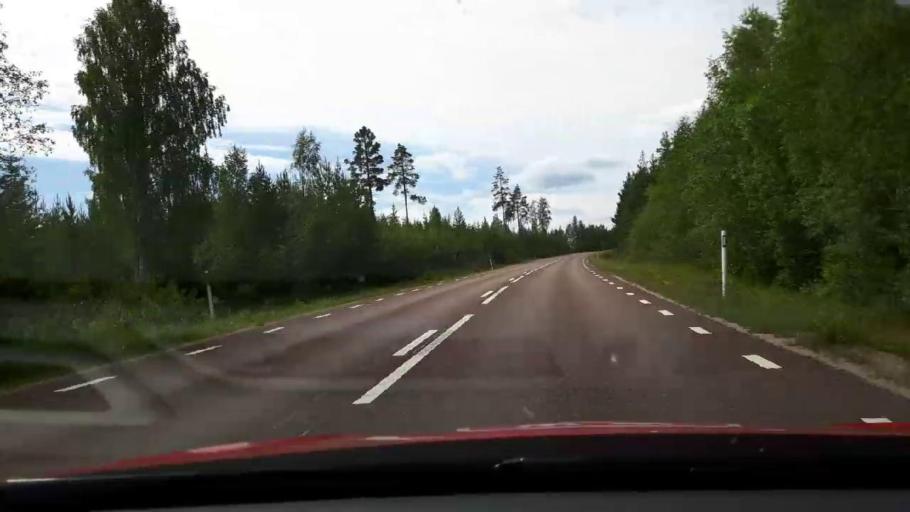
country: SE
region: Jaemtland
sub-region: Harjedalens Kommun
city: Sveg
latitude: 62.0506
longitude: 14.8948
